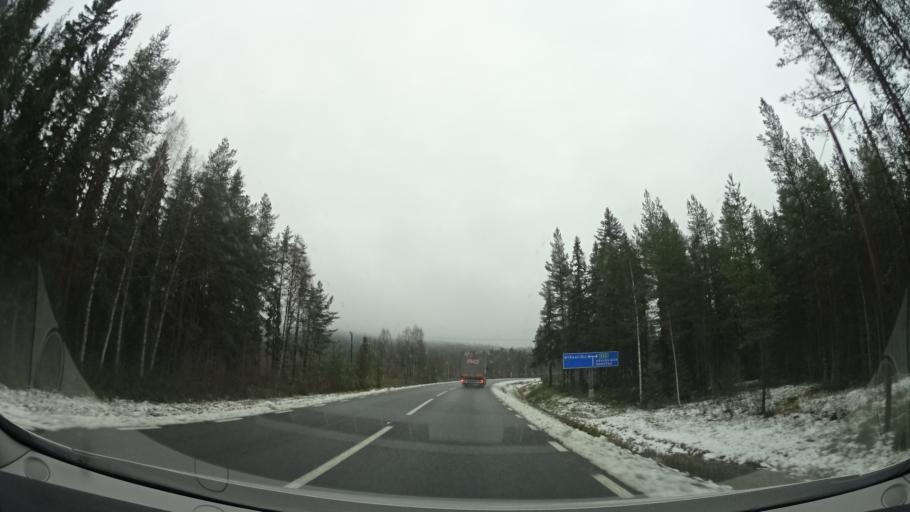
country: SE
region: Vaesterbotten
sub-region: Dorotea Kommun
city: Dorotea
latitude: 64.2567
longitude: 16.3714
